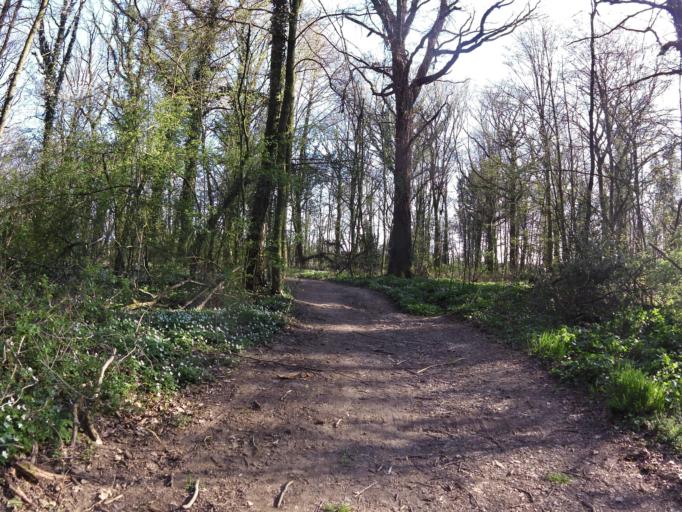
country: DE
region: Bavaria
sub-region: Regierungsbezirk Unterfranken
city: Kurnach
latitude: 49.8261
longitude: 10.0603
